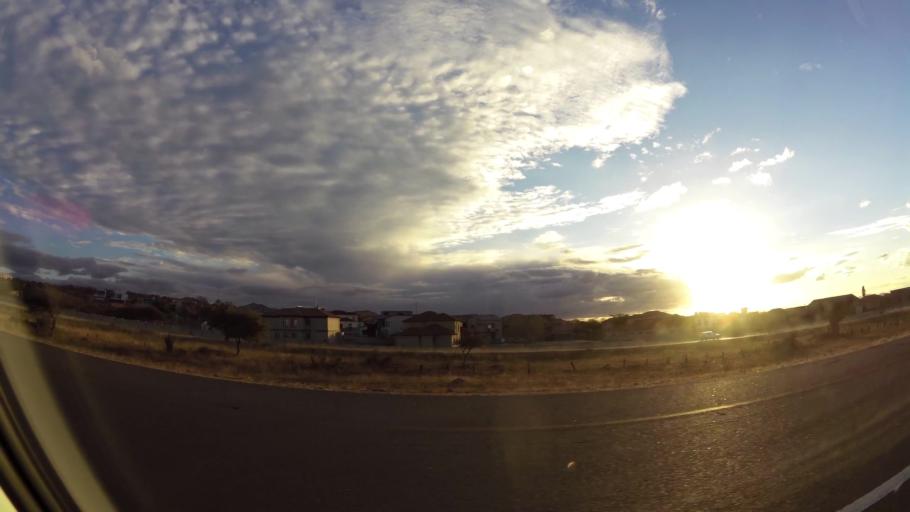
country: ZA
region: Limpopo
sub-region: Capricorn District Municipality
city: Polokwane
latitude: -23.8863
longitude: 29.5085
